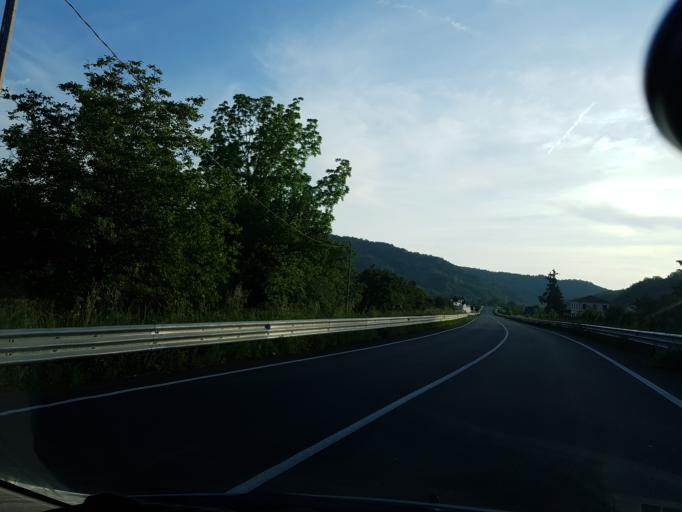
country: IT
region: Tuscany
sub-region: Provincia di Massa-Carrara
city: Fivizzano
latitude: 44.2031
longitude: 10.0948
